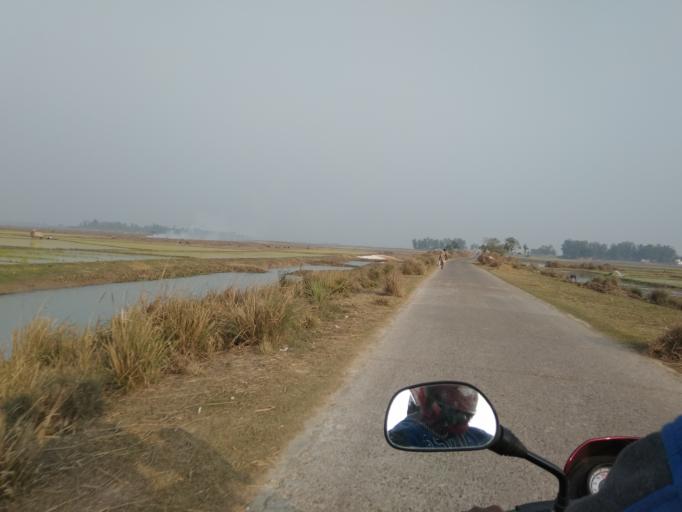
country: BD
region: Rajshahi
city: Ishurdi
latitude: 24.4948
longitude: 89.1932
